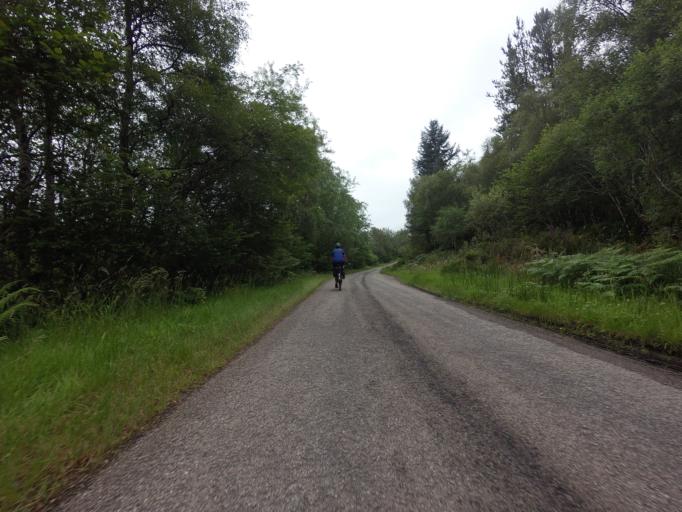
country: GB
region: Scotland
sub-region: Highland
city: Evanton
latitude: 57.9629
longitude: -4.4085
